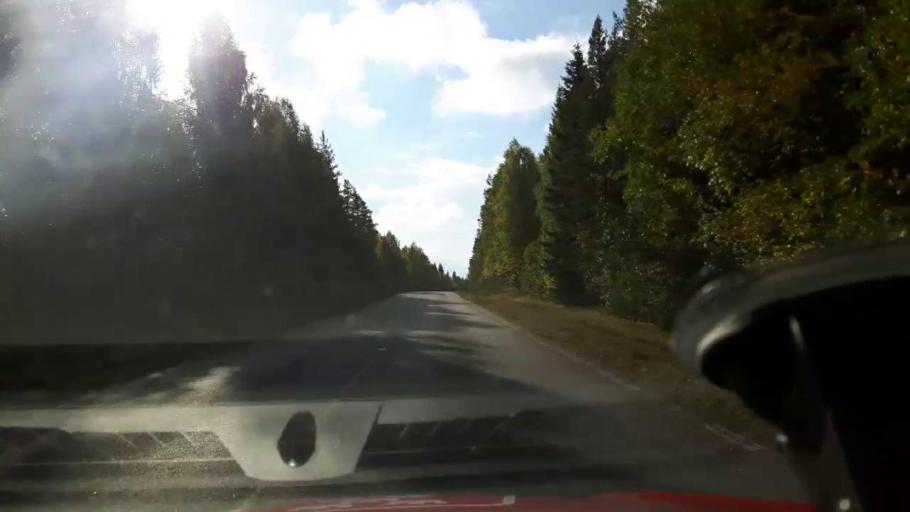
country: SE
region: Vaesternorrland
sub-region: Ange Kommun
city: Ange
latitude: 62.0812
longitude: 15.0978
